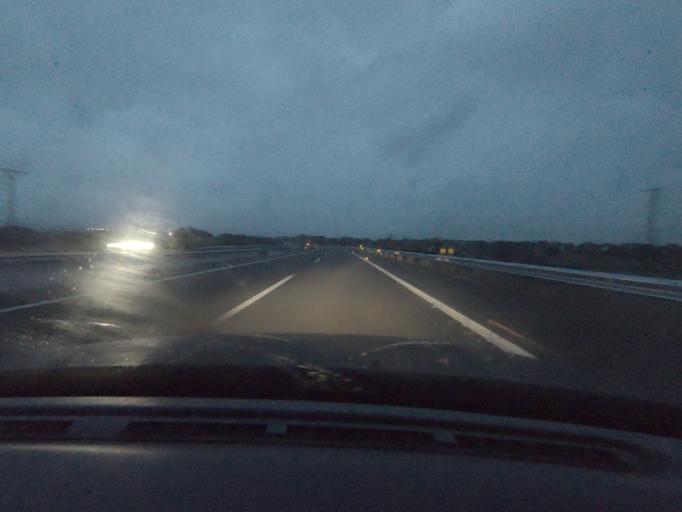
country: ES
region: Extremadura
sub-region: Provincia de Caceres
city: Aldea del Cano
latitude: 39.3545
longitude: -6.3405
